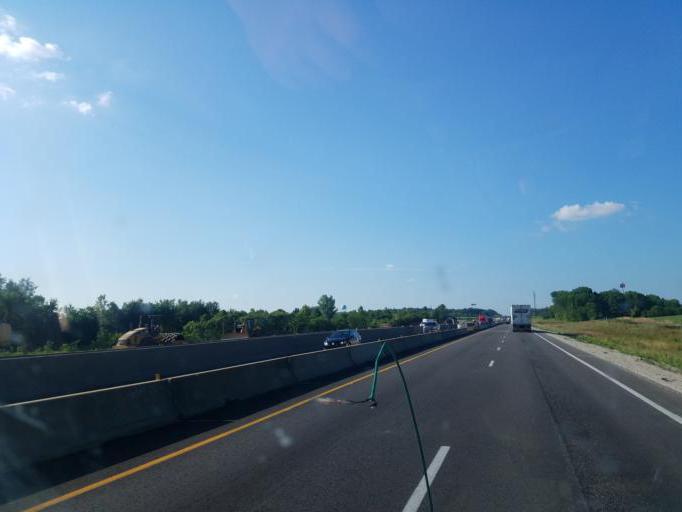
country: US
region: Kentucky
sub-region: Hardin County
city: Elizabethtown
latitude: 37.5877
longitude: -85.8704
